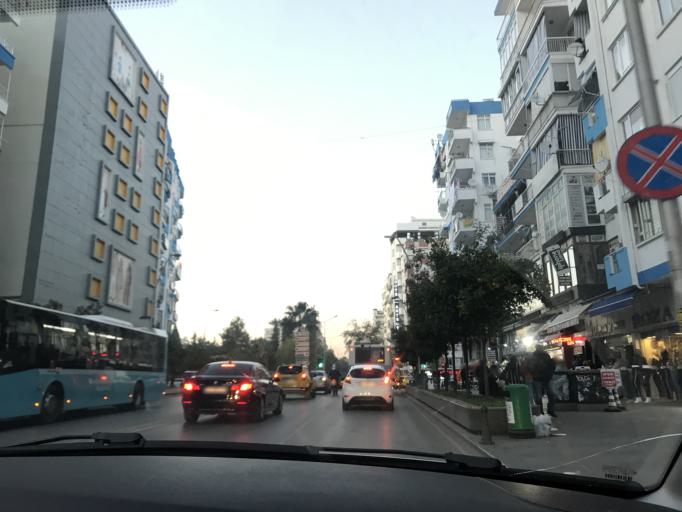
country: TR
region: Antalya
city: Antalya
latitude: 36.8903
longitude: 30.6951
